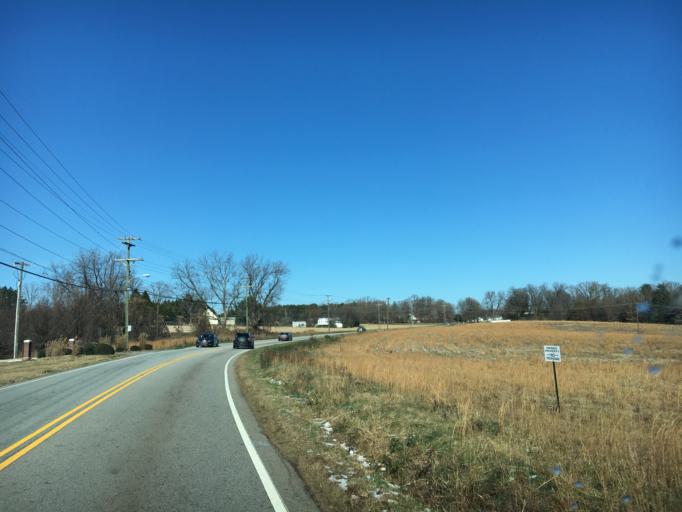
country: US
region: South Carolina
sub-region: Greenville County
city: Taylors
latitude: 34.9197
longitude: -82.2686
